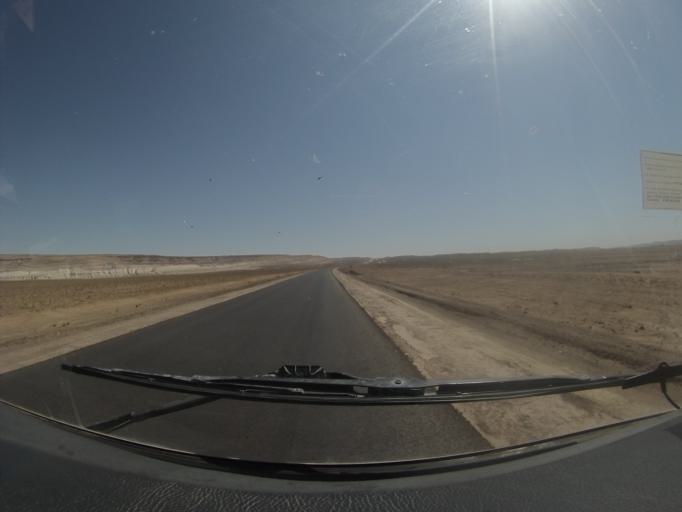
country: KZ
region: Mangghystau
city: Omirzaq
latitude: 43.6030
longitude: 51.2250
